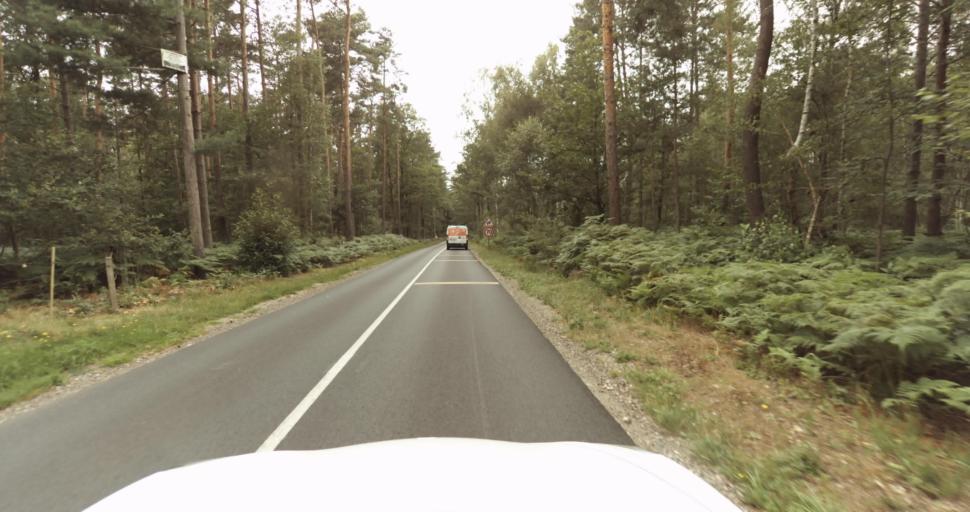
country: FR
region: Haute-Normandie
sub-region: Departement de l'Eure
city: Saint-Sebastien-de-Morsent
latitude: 48.9876
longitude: 1.0588
